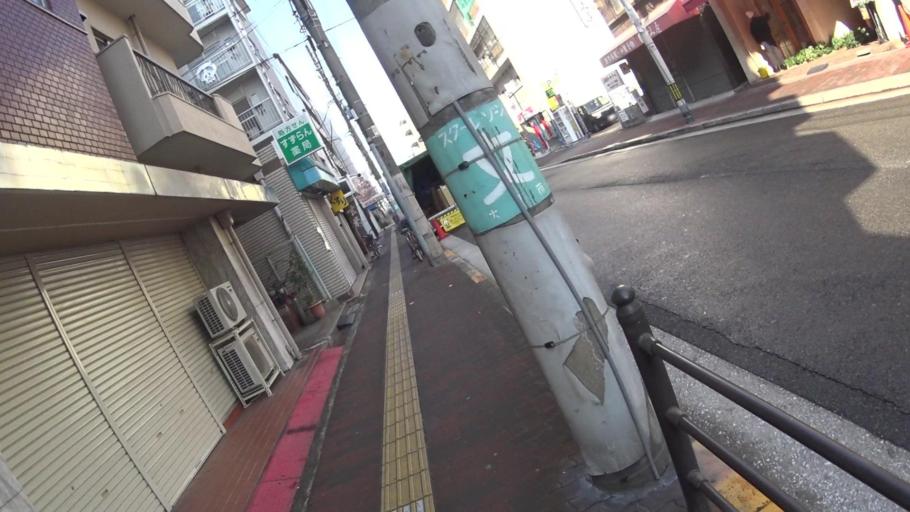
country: JP
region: Osaka
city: Sakai
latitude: 34.6014
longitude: 135.5112
